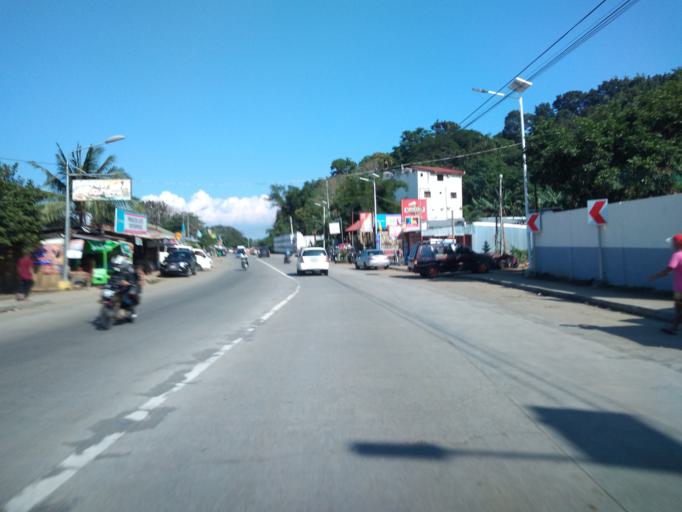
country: PH
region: Calabarzon
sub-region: Province of Laguna
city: Calamba
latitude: 14.1855
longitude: 121.1642
